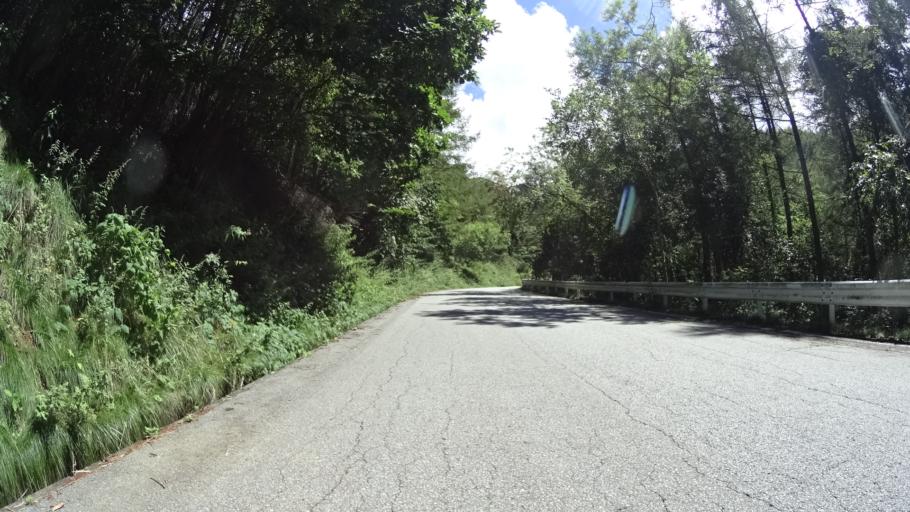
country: JP
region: Yamanashi
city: Enzan
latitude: 35.7216
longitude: 138.8421
